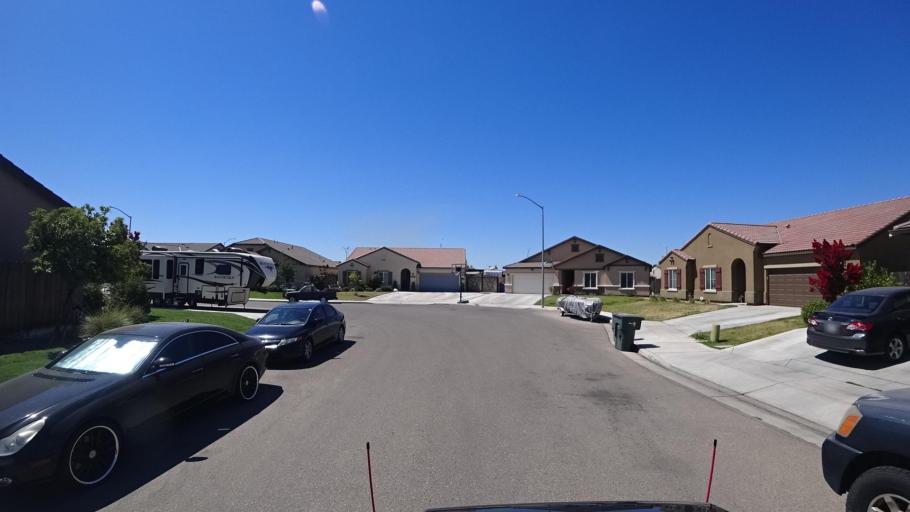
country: US
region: California
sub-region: Fresno County
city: Sunnyside
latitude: 36.7215
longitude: -119.6693
